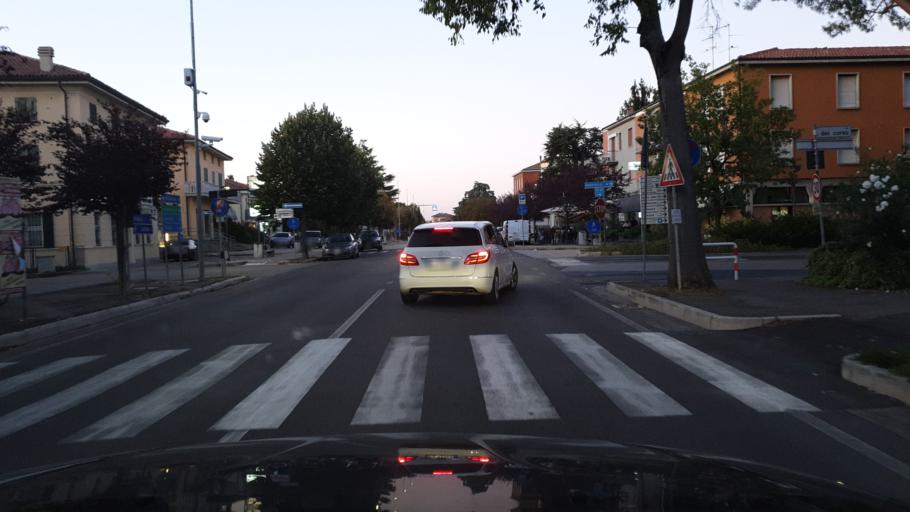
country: IT
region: Emilia-Romagna
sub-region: Provincia di Bologna
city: Altedo
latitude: 44.6645
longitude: 11.4866
